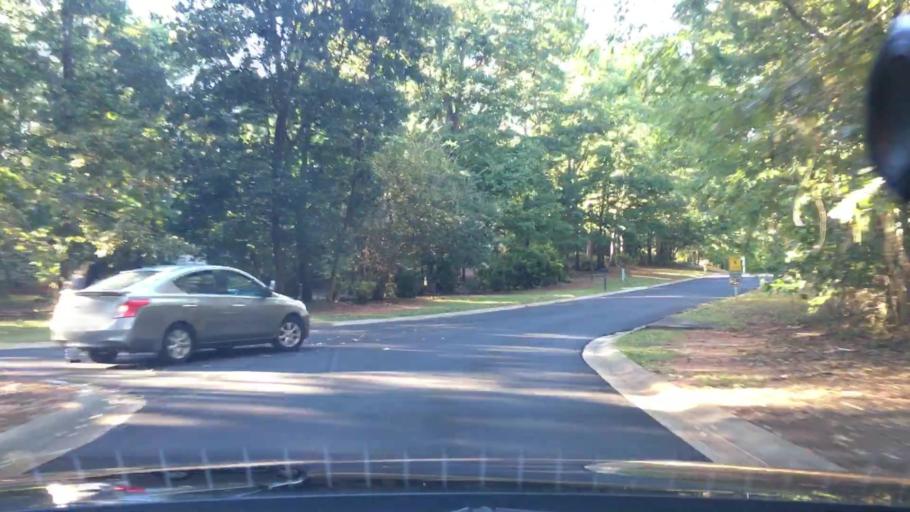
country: US
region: Georgia
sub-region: Coweta County
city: East Newnan
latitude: 33.4126
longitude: -84.7055
